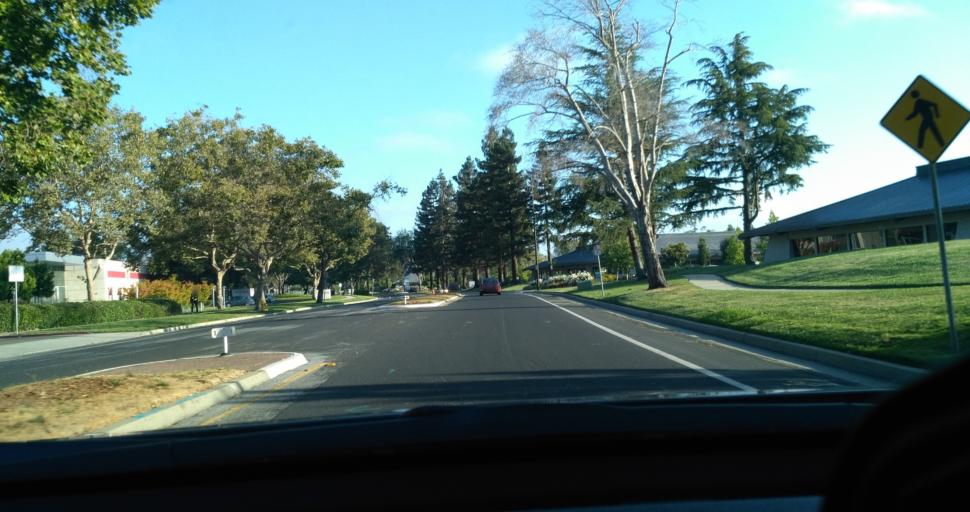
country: US
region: California
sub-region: Santa Clara County
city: Santa Clara
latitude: 37.3865
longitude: -121.9330
